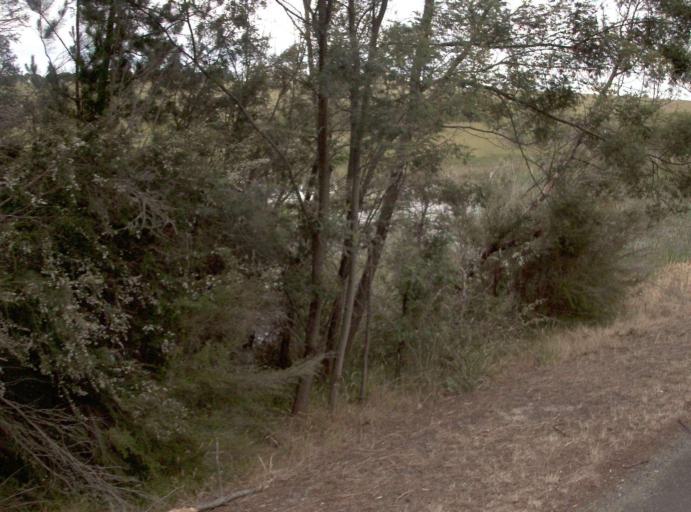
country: AU
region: Victoria
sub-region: Wellington
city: Sale
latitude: -38.2073
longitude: 147.0696
